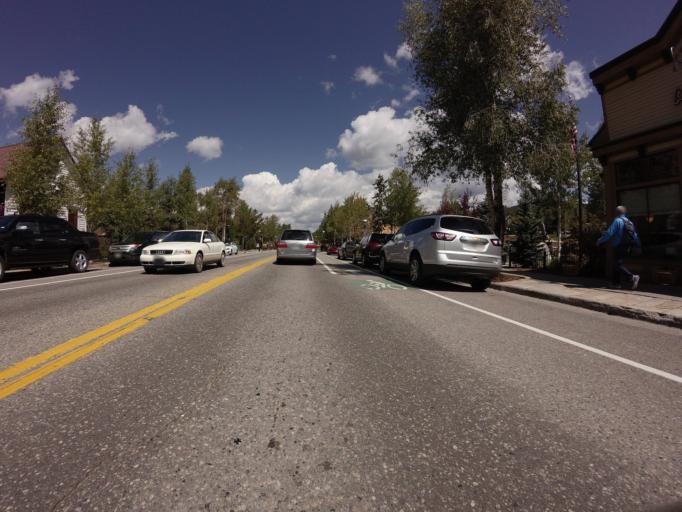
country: US
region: Colorado
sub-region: Summit County
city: Breckenridge
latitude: 39.4829
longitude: -106.0462
